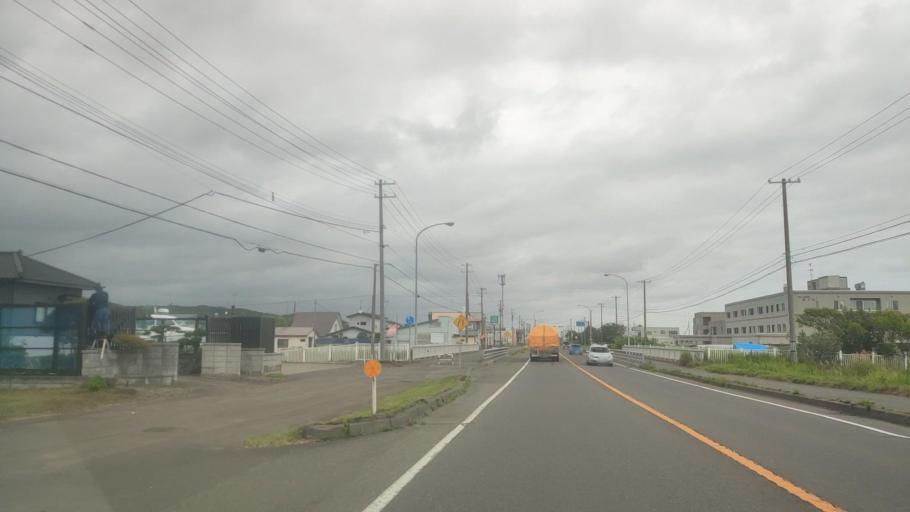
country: JP
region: Hokkaido
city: Shiraoi
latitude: 42.5154
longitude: 141.2992
